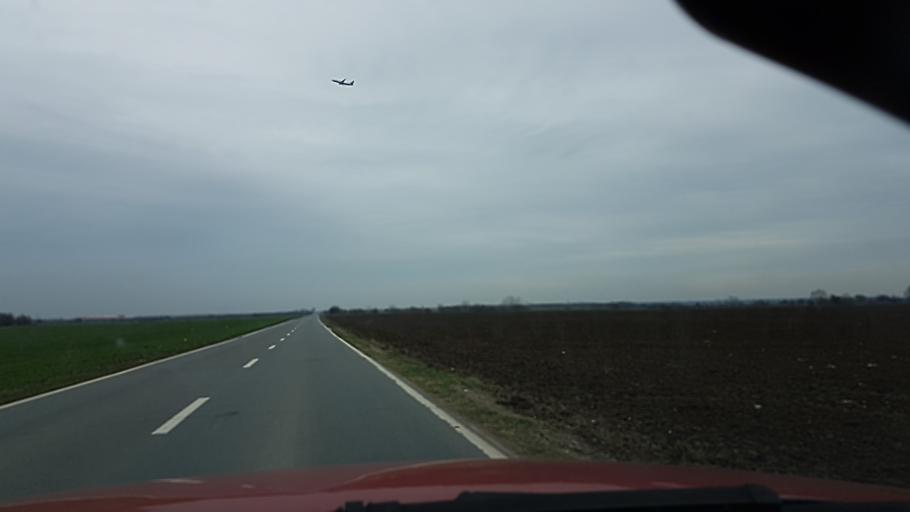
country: RO
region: Ilfov
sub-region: Comuna Tunari
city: Tunari
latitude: 44.5803
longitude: 26.1389
